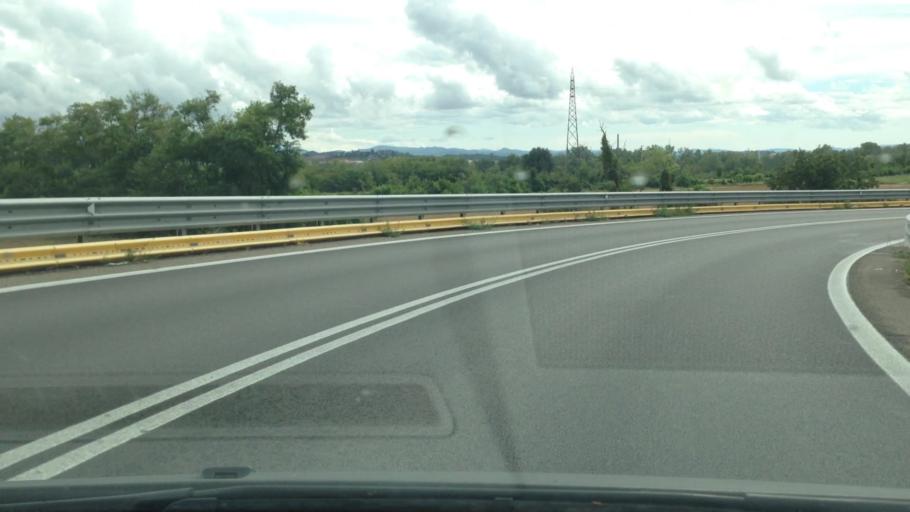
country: IT
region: Piedmont
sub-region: Provincia di Alessandria
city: Tortona
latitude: 44.9083
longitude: 8.8455
